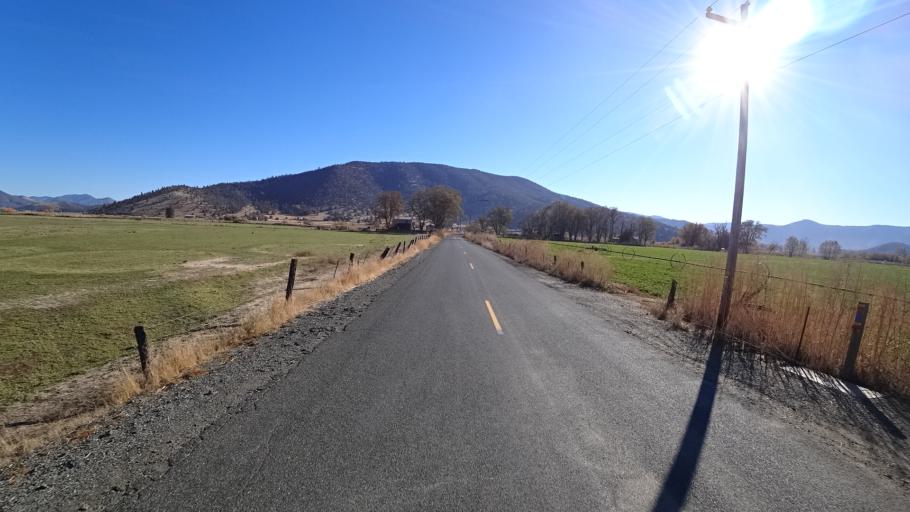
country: US
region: California
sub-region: Siskiyou County
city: Yreka
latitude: 41.5193
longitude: -122.8536
